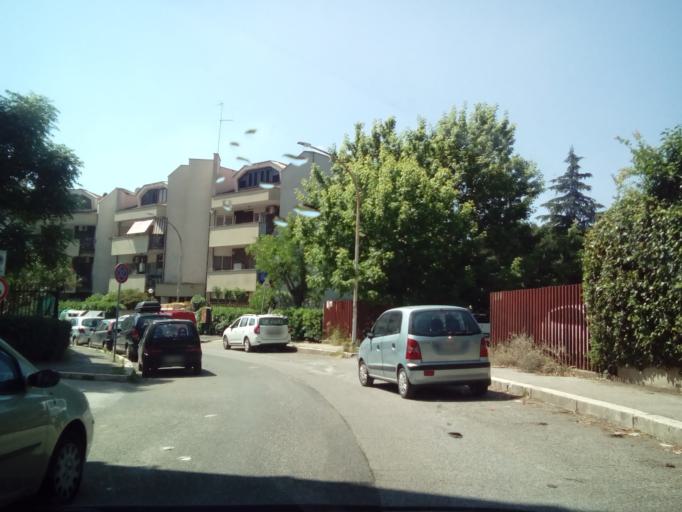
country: IT
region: Latium
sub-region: Citta metropolitana di Roma Capitale
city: Rome
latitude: 41.8864
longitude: 12.5842
